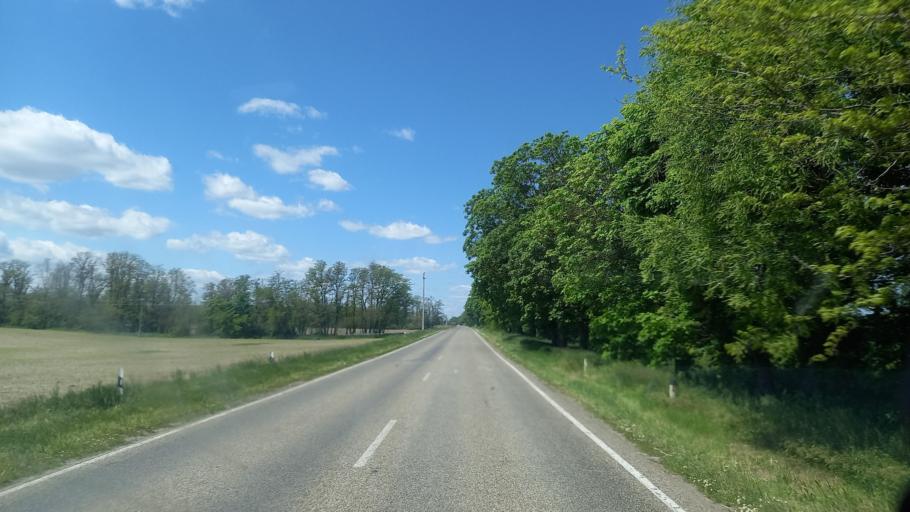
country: RU
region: Krasnodarskiy
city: Kazanskaya
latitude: 45.3653
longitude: 40.4010
